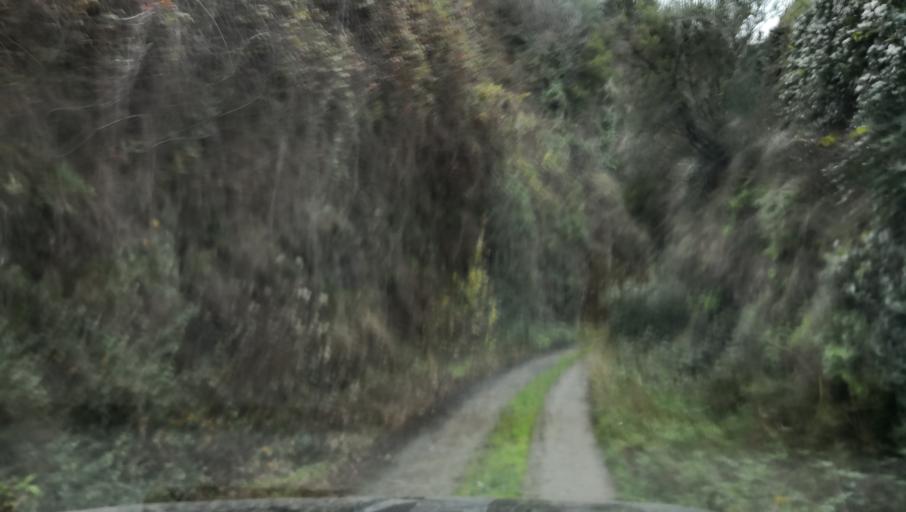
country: PT
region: Vila Real
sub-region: Vila Real
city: Vila Real
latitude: 41.2397
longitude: -7.7406
